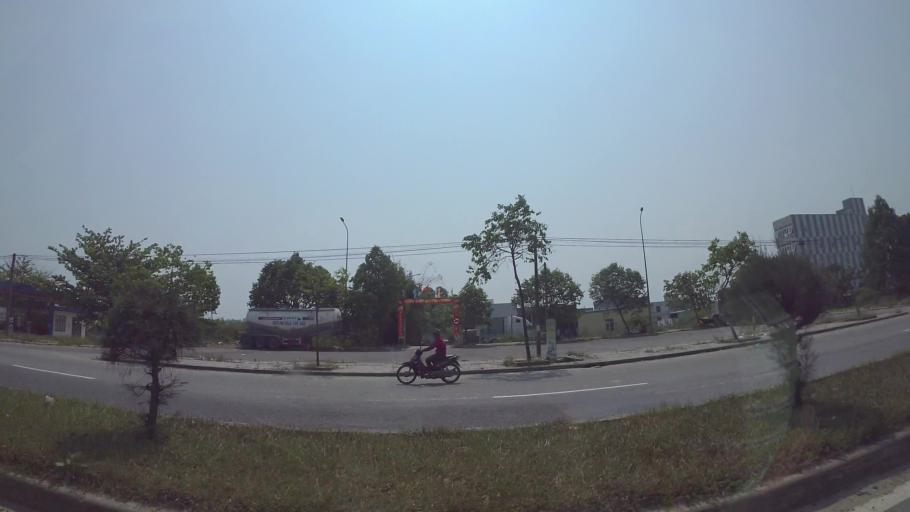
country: VN
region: Da Nang
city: Cam Le
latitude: 15.9831
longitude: 108.2051
